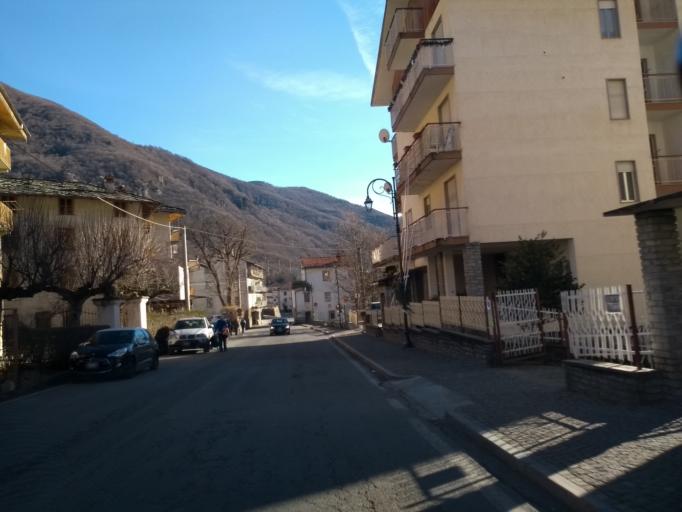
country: IT
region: Piedmont
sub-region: Provincia di Torino
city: Cantoira
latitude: 45.3420
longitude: 7.3816
